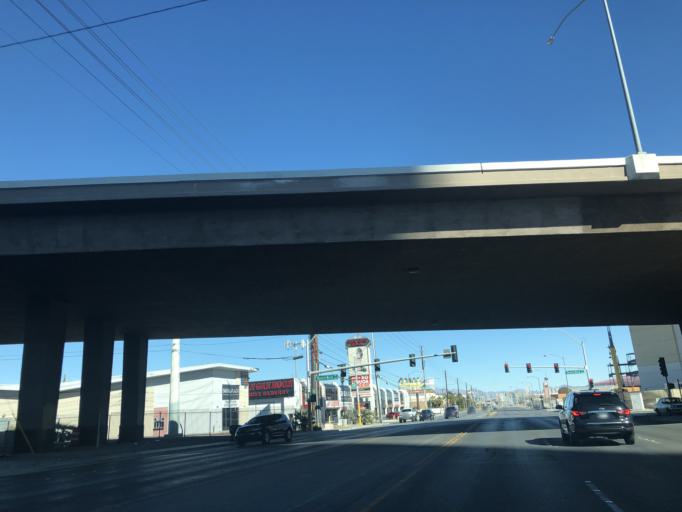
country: US
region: Nevada
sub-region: Clark County
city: Paradise
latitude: 36.1312
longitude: -115.1732
